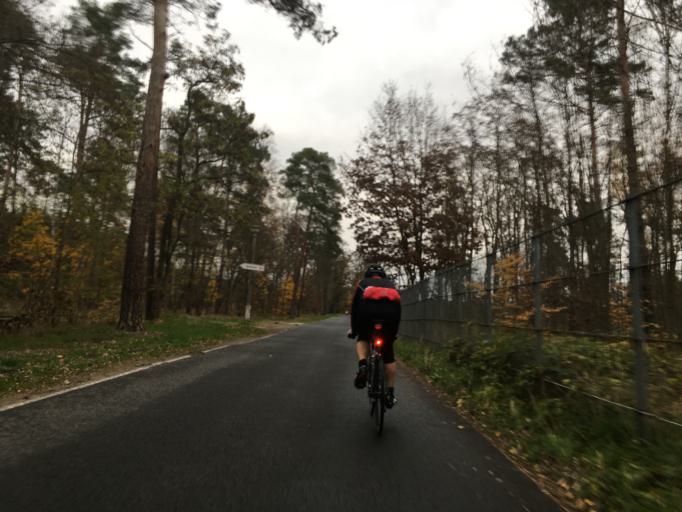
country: DE
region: Brandenburg
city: Gross Lindow
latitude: 52.2772
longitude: 14.4867
